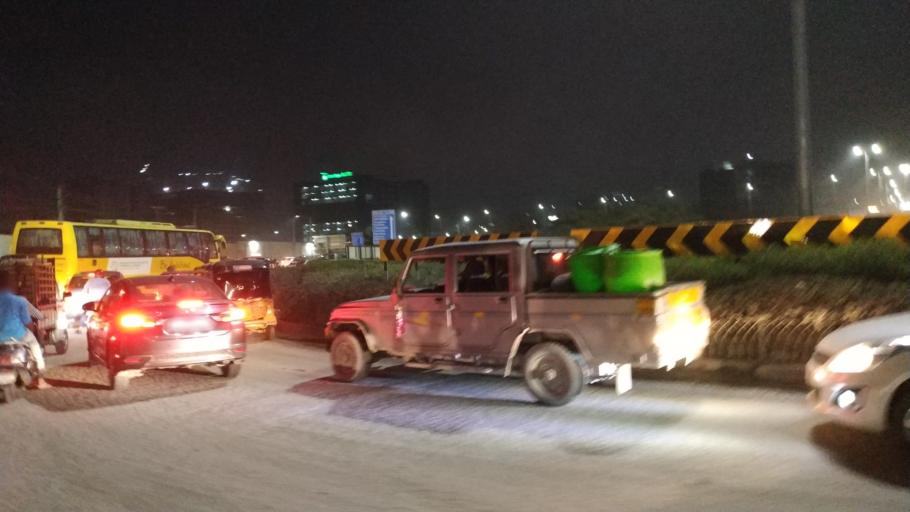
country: IN
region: Telangana
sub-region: Rangareddi
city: Kukatpalli
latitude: 17.4186
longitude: 78.3585
